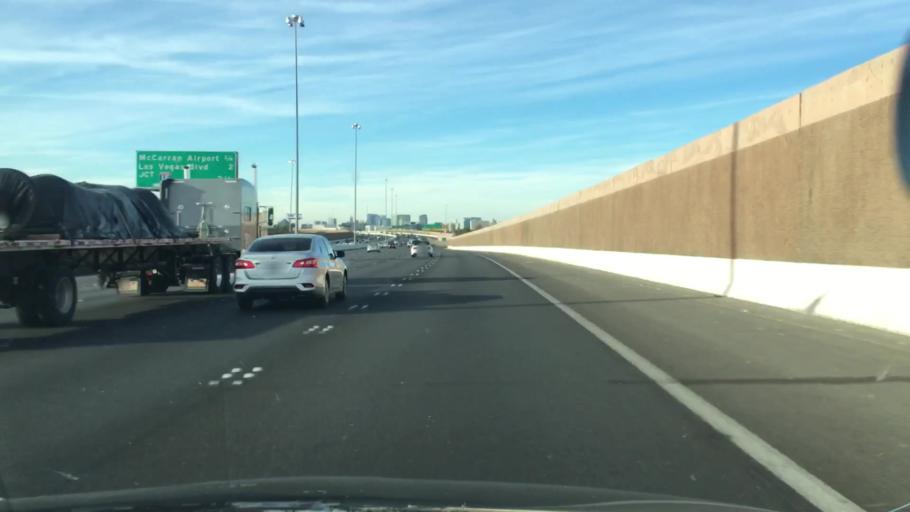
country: US
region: Nevada
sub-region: Clark County
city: Paradise
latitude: 36.0513
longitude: -115.1361
